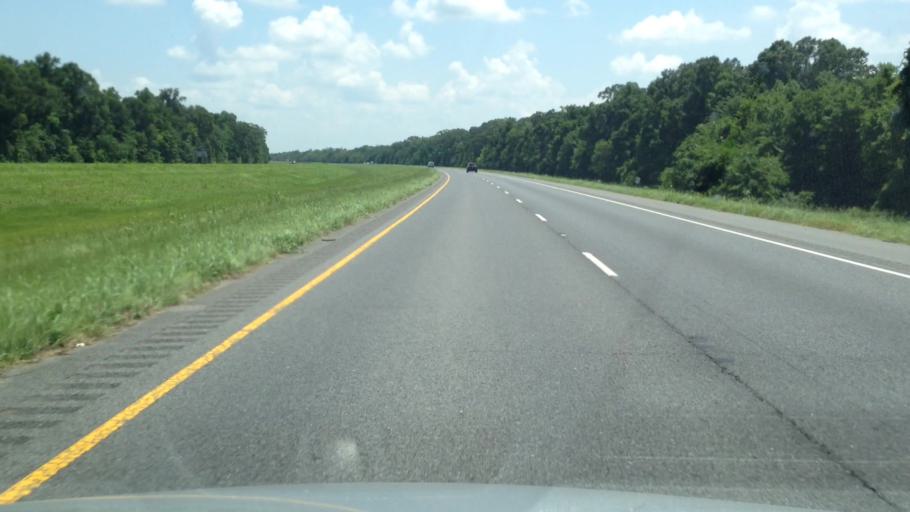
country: US
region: Louisiana
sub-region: Avoyelles Parish
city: Bunkie
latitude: 30.8409
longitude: -92.2292
